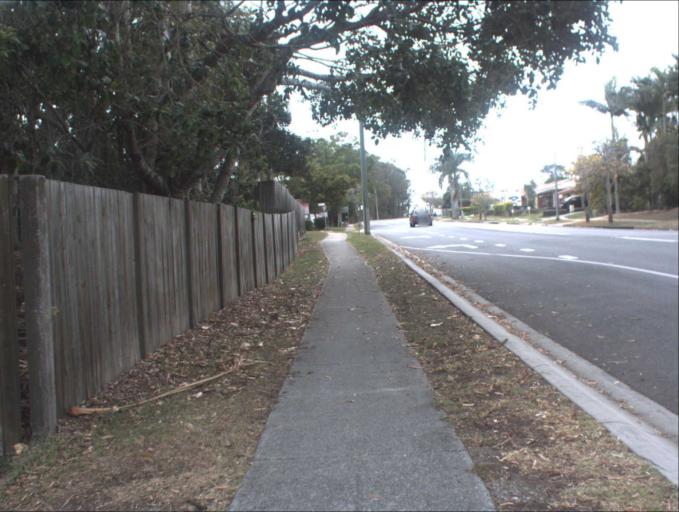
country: AU
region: Queensland
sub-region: Logan
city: Slacks Creek
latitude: -27.6761
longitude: 153.1813
